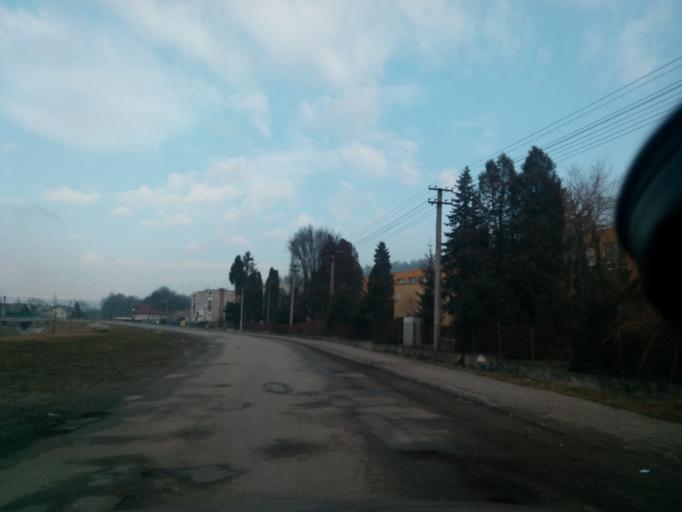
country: SK
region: Presovsky
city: Lipany
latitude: 49.1745
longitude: 20.8700
